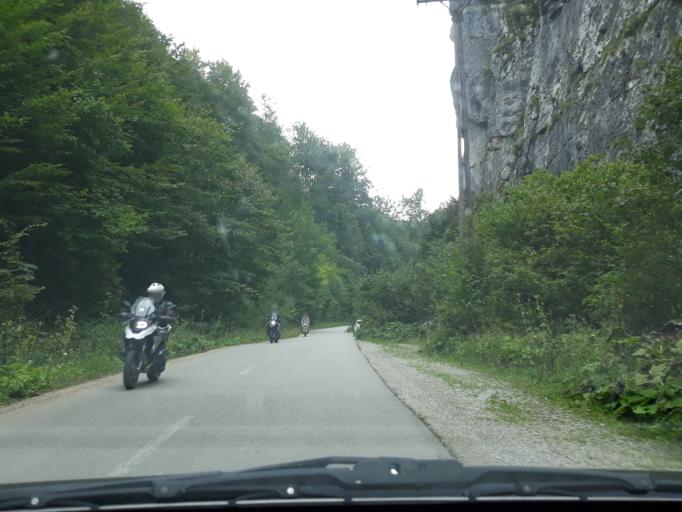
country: RO
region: Bihor
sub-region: Comuna Pietroasa
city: Pietroasa
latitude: 46.6016
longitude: 22.6424
